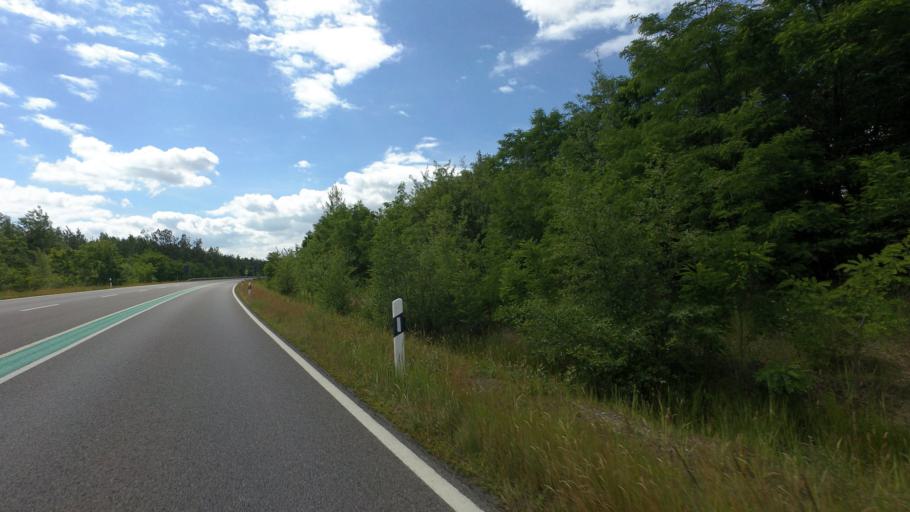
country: DE
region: Brandenburg
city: Senftenberg
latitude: 51.5314
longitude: 13.9862
